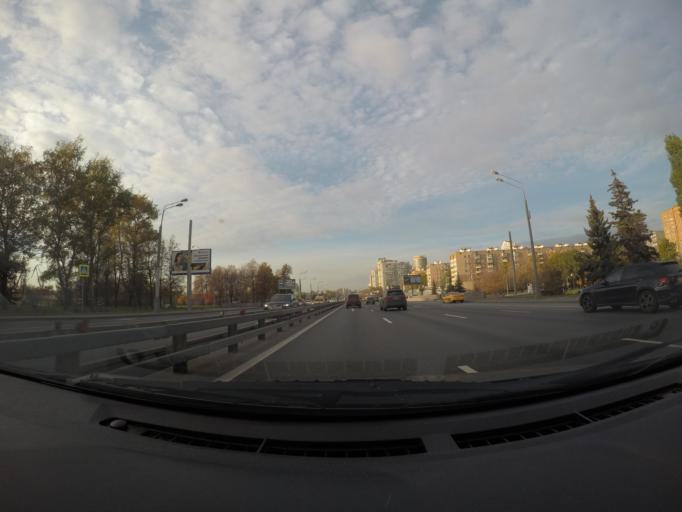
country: RU
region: Moskovskaya
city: Levoberezhnyy
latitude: 55.8618
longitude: 37.4659
